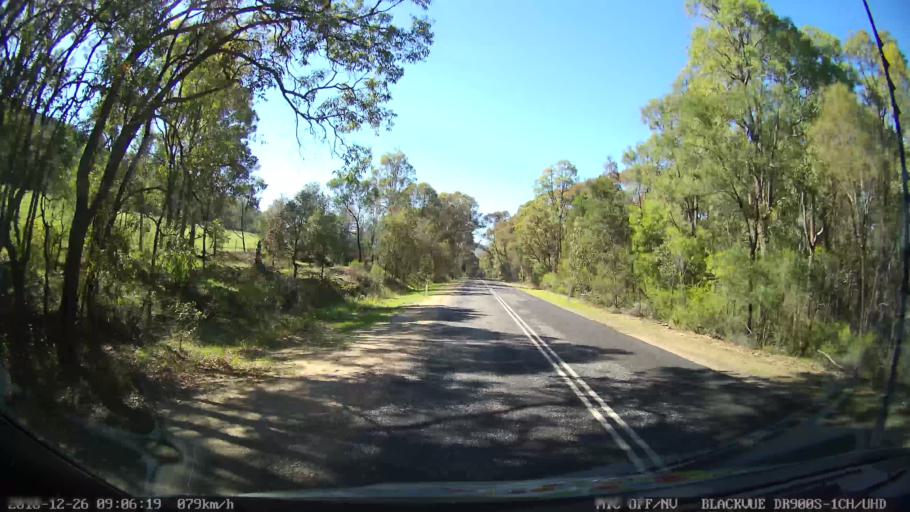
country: AU
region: New South Wales
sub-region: Mid-Western Regional
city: Kandos
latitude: -32.6928
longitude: 150.0050
